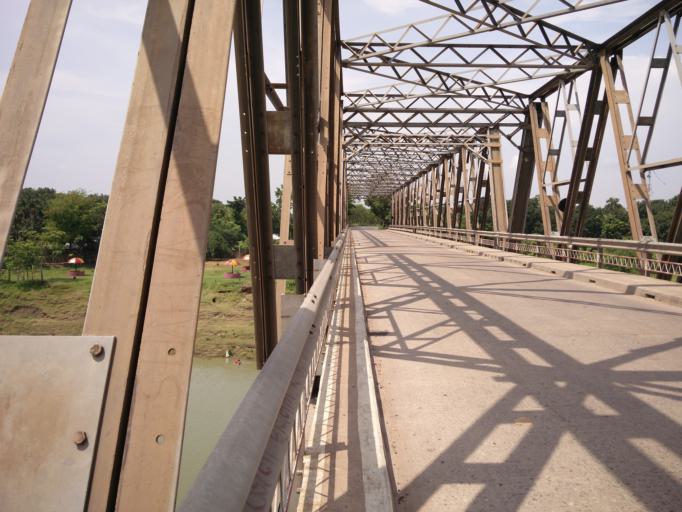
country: BD
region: Khulna
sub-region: Magura
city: Magura
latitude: 23.5409
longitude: 89.5167
